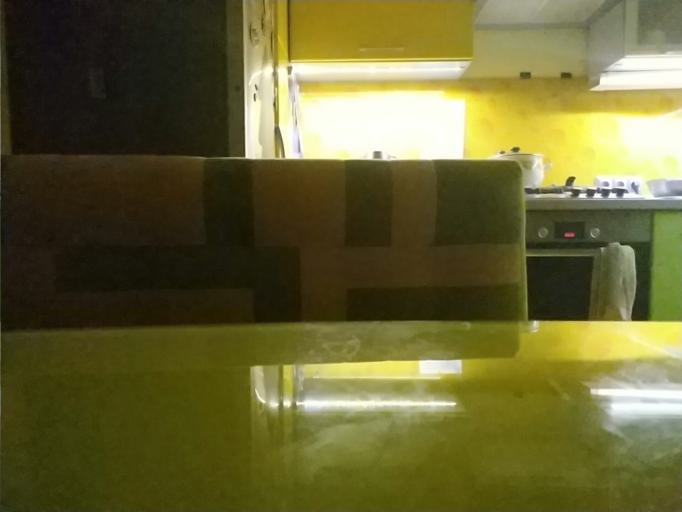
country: RU
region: Republic of Karelia
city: Pyaozerskiy
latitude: 65.8525
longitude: 30.4490
